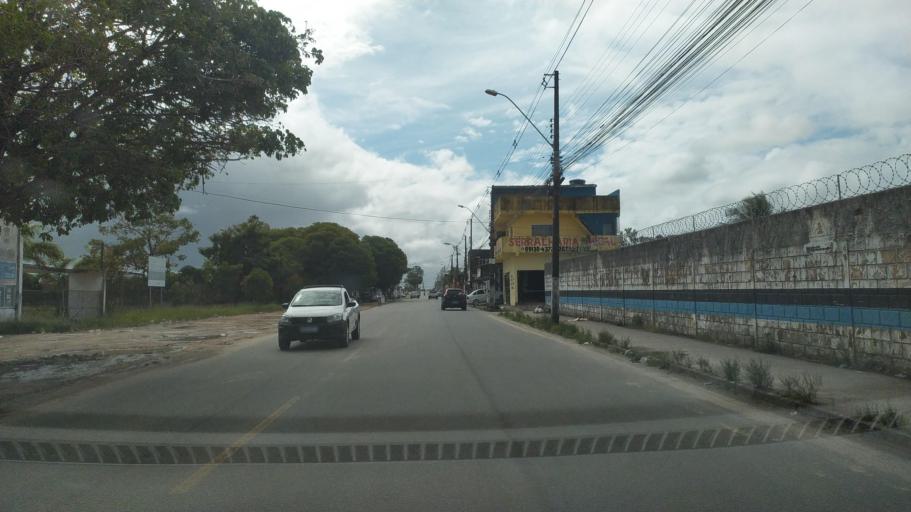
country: BR
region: Alagoas
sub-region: Satuba
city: Satuba
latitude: -9.5493
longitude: -35.7599
